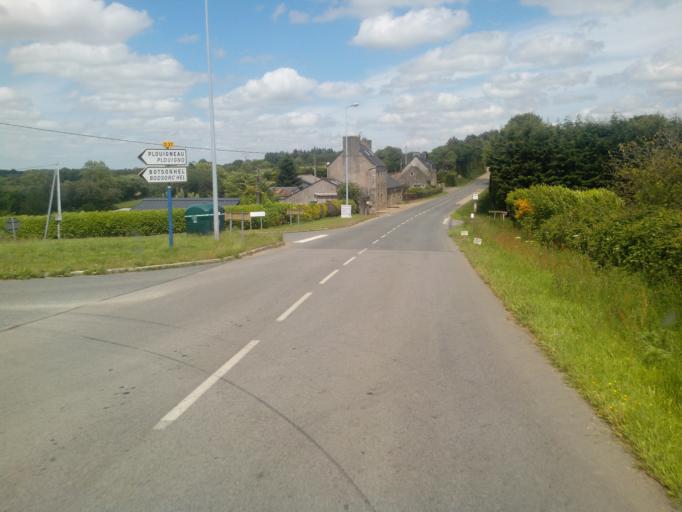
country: FR
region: Brittany
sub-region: Departement du Finistere
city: Guerlesquin
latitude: 48.5007
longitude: -3.6137
